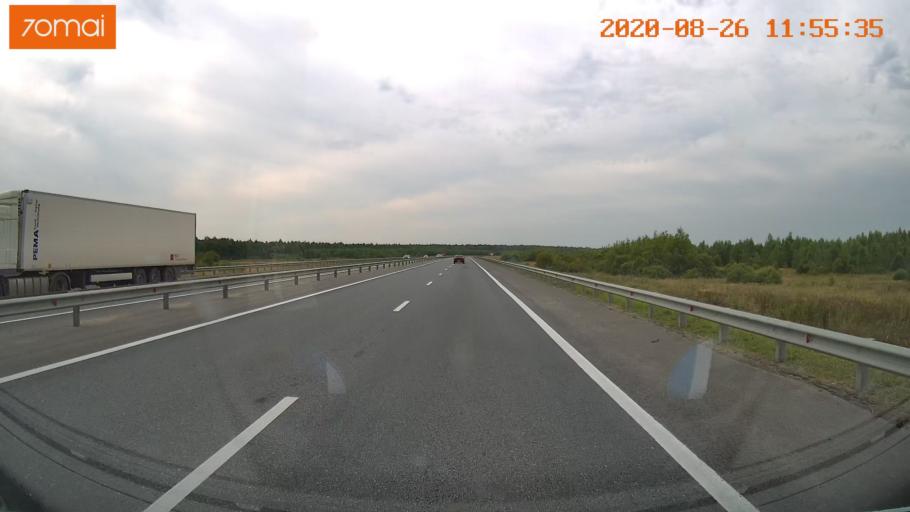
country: RU
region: Rjazan
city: Kiritsy
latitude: 54.2711
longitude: 40.3938
